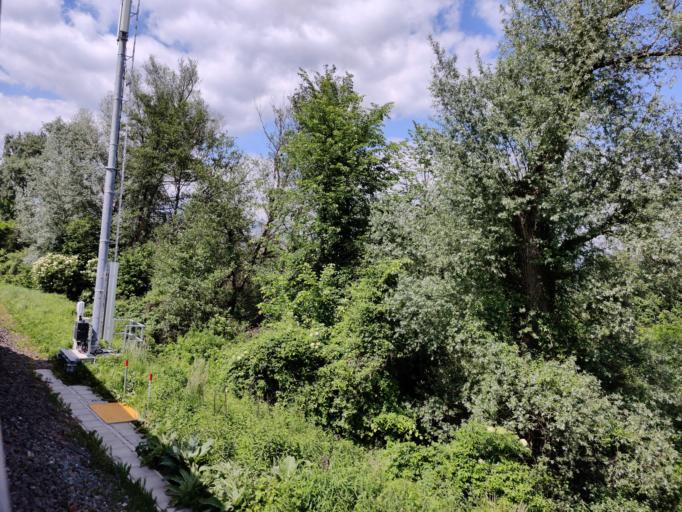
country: AT
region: Styria
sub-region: Politischer Bezirk Leibnitz
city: Stocking
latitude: 46.8766
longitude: 15.5294
